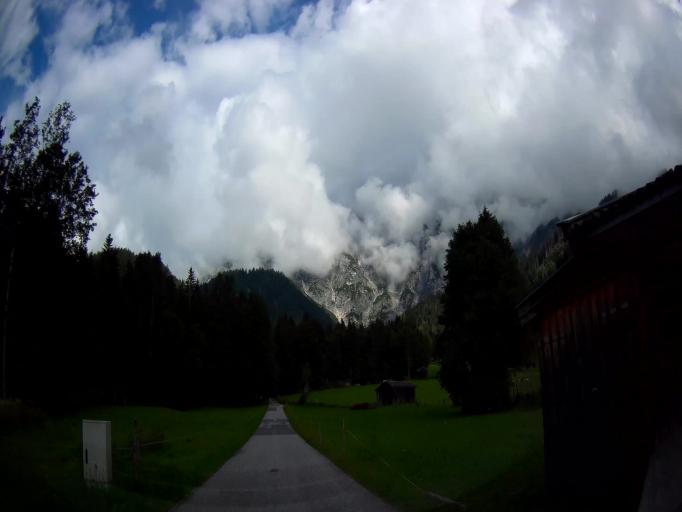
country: AT
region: Salzburg
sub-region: Politischer Bezirk Zell am See
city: Leogang
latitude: 47.4507
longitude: 12.7599
